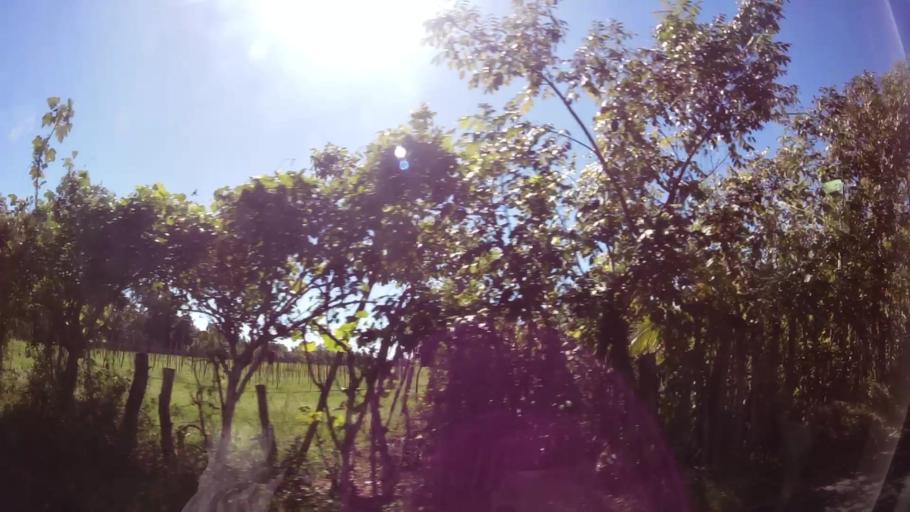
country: GT
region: Escuintla
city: Iztapa
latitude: 13.9333
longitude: -90.6936
